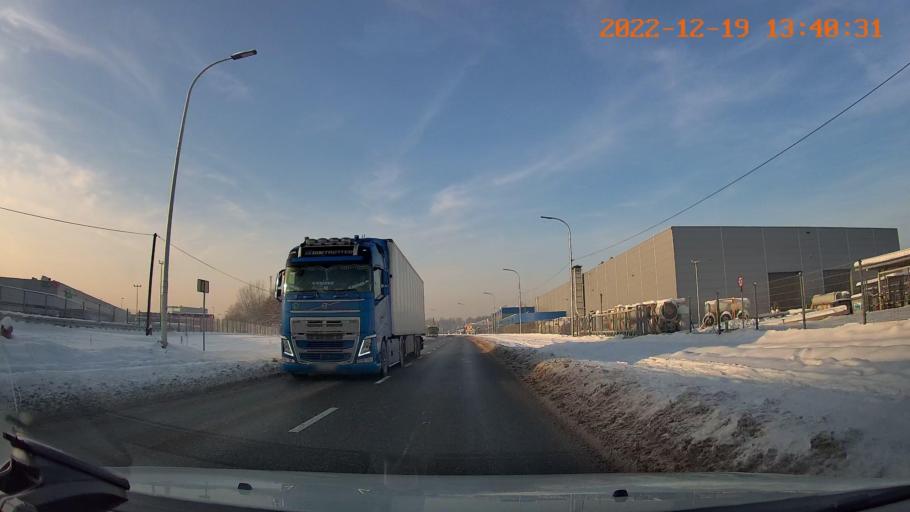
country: PL
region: Silesian Voivodeship
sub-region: Tychy
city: Cielmice
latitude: 50.1029
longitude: 19.0406
